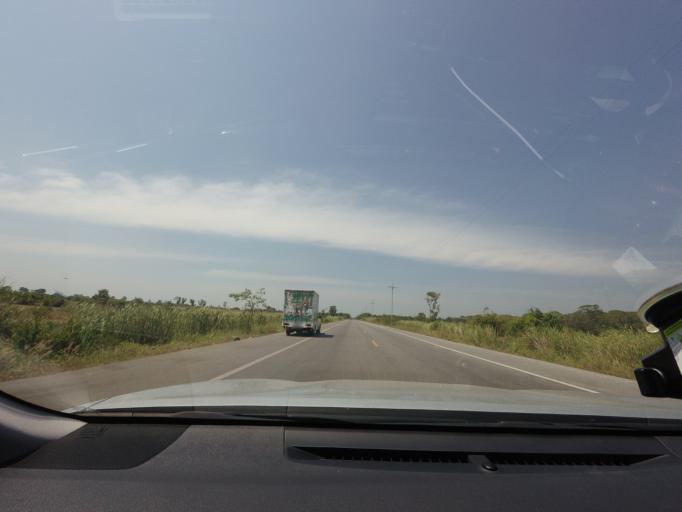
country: TH
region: Surat Thani
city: Tha Chang
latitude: 9.2206
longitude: 99.2149
